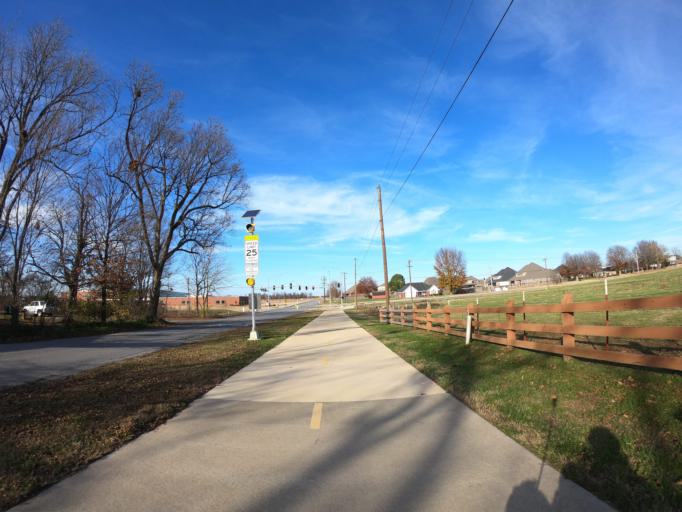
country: US
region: Arkansas
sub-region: Benton County
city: Lowell
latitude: 36.2682
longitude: -94.1635
